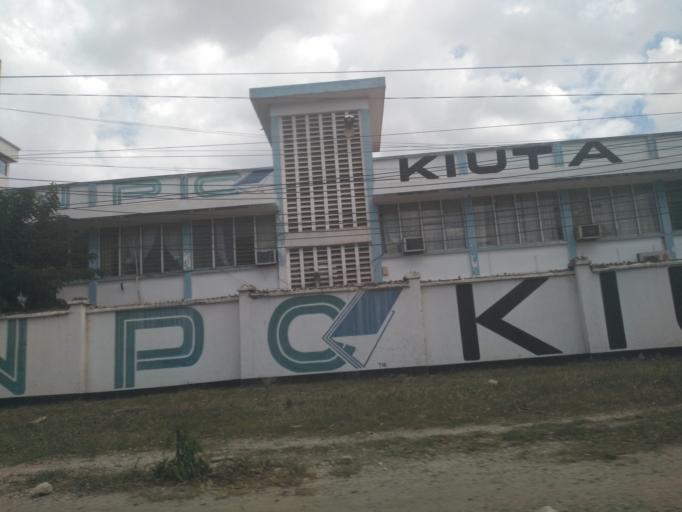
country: TZ
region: Dar es Salaam
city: Dar es Salaam
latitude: -6.8382
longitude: 39.2584
